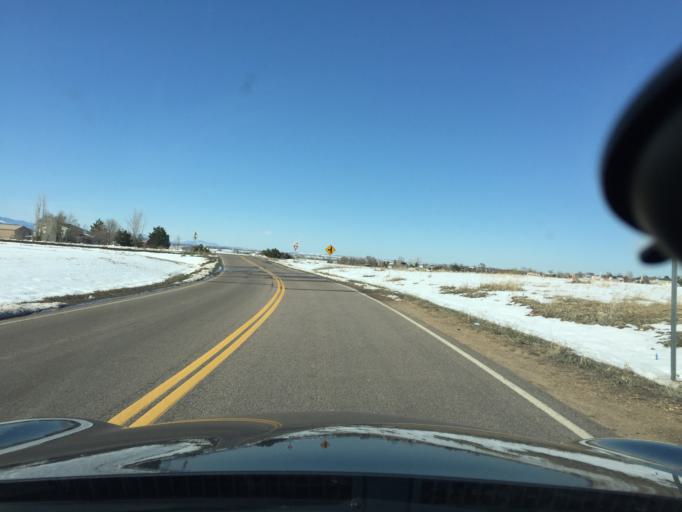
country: US
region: Colorado
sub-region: Boulder County
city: Erie
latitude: 40.0610
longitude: -105.0371
